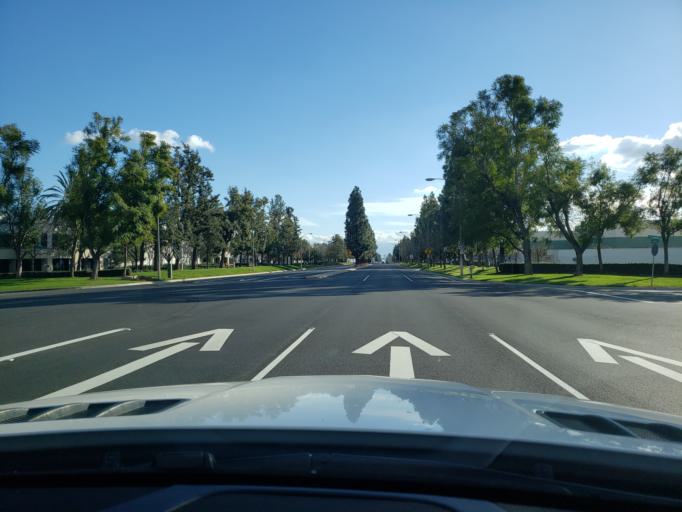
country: US
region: California
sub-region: San Bernardino County
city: Rancho Cucamonga
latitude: 34.0521
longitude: -117.5583
